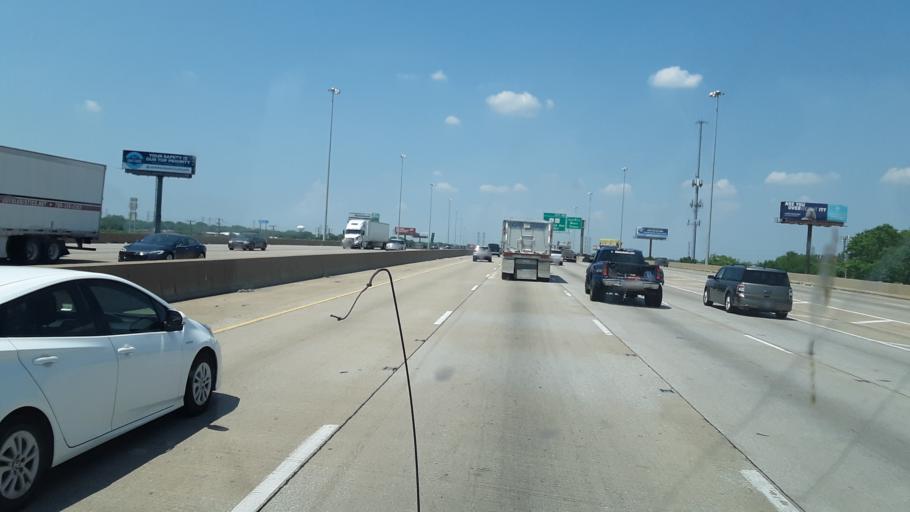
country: US
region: Illinois
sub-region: Cook County
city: Lansing
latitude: 41.5786
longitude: -87.5455
